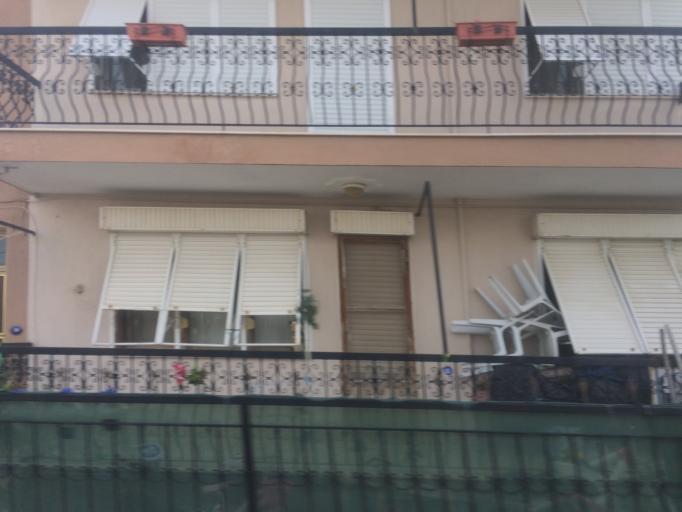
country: TR
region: Izmir
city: Karsiyaka
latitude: 38.4926
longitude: 26.9477
